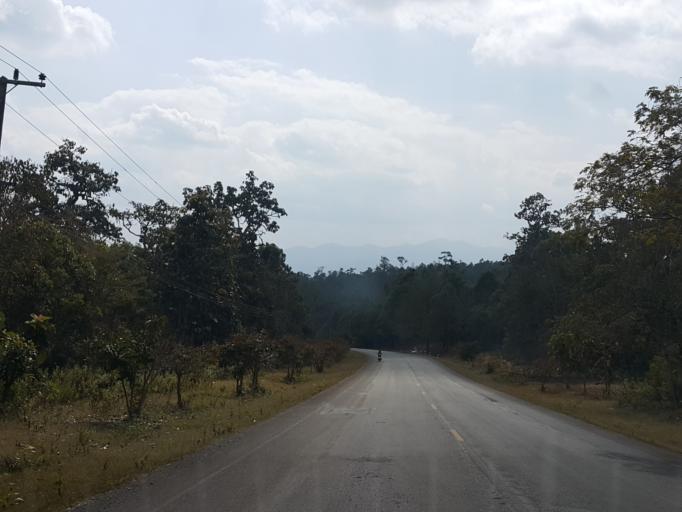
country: TH
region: Chiang Mai
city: Om Koi
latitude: 17.8567
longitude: 98.3720
